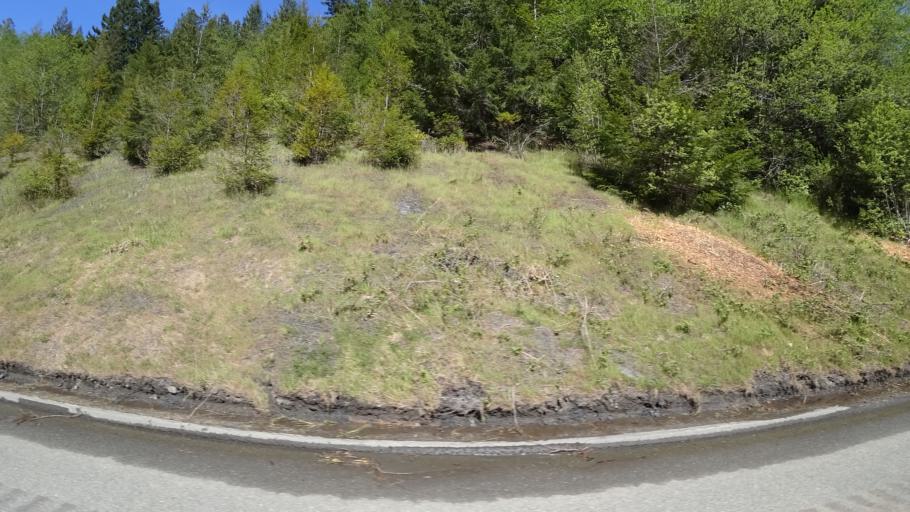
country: US
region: California
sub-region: Del Norte County
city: Bertsch-Oceanview
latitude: 41.4163
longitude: -123.9989
